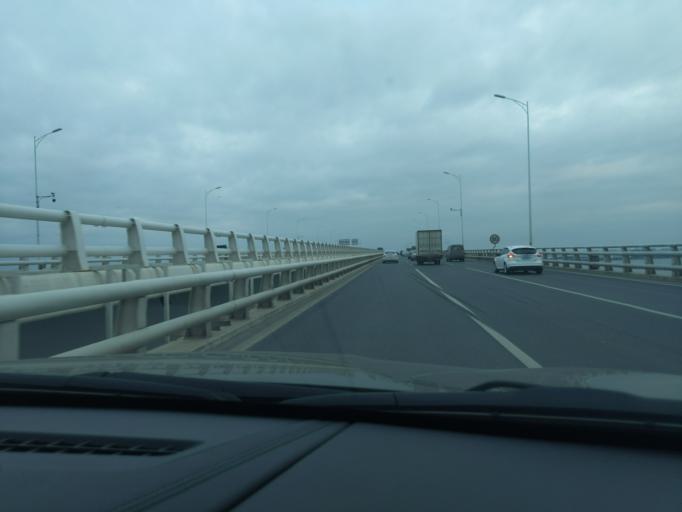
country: CN
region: Fujian
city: Yingcun
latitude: 24.5816
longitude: 118.1135
